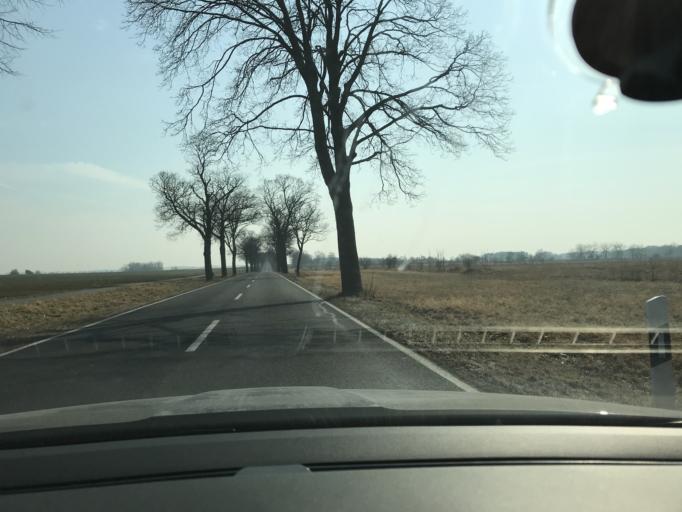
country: DE
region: Brandenburg
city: Mittenwalde
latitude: 52.2992
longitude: 13.5174
